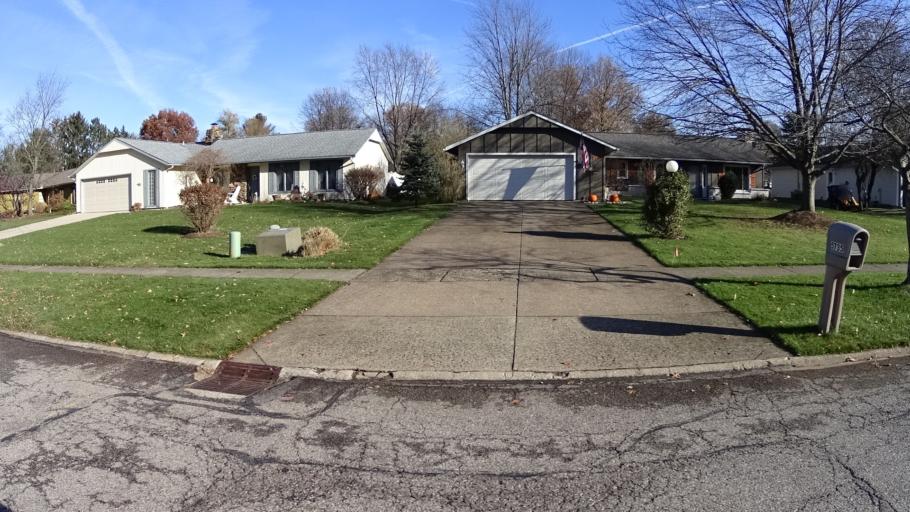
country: US
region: Ohio
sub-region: Lorain County
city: North Ridgeville
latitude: 41.4035
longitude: -81.9817
